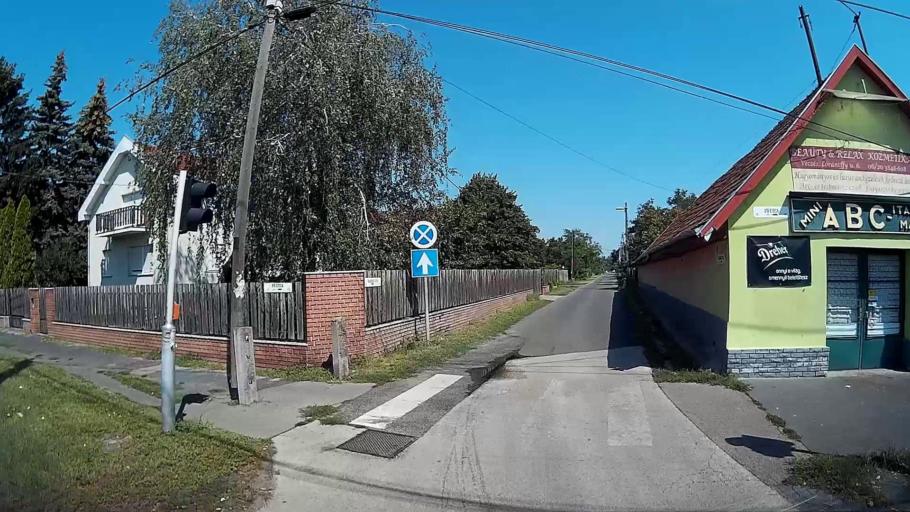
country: HU
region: Pest
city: Vecses
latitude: 47.4111
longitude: 19.2724
